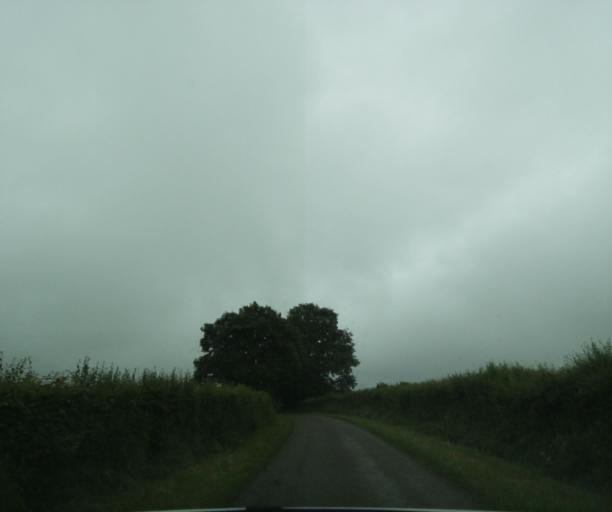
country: FR
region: Bourgogne
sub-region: Departement de Saone-et-Loire
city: Charolles
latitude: 46.4609
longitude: 4.2302
